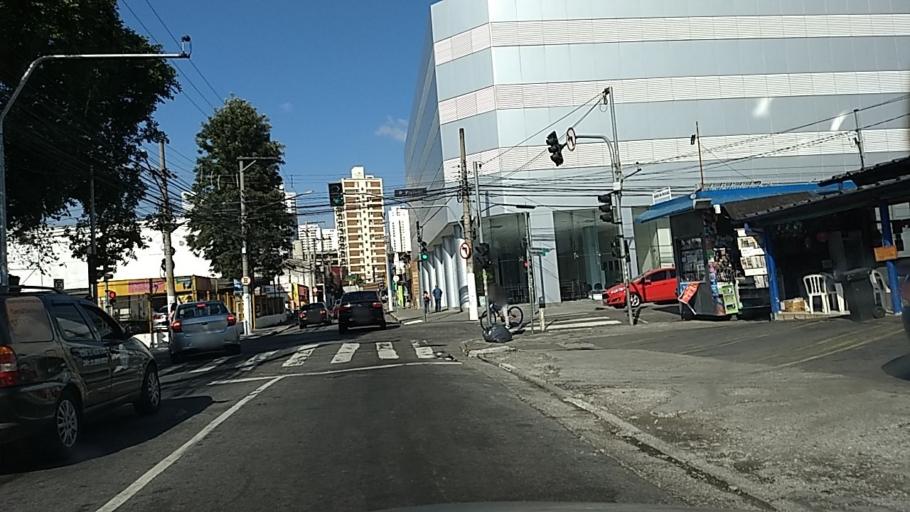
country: BR
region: Sao Paulo
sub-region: Osasco
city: Osasco
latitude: -23.5328
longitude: -46.7771
